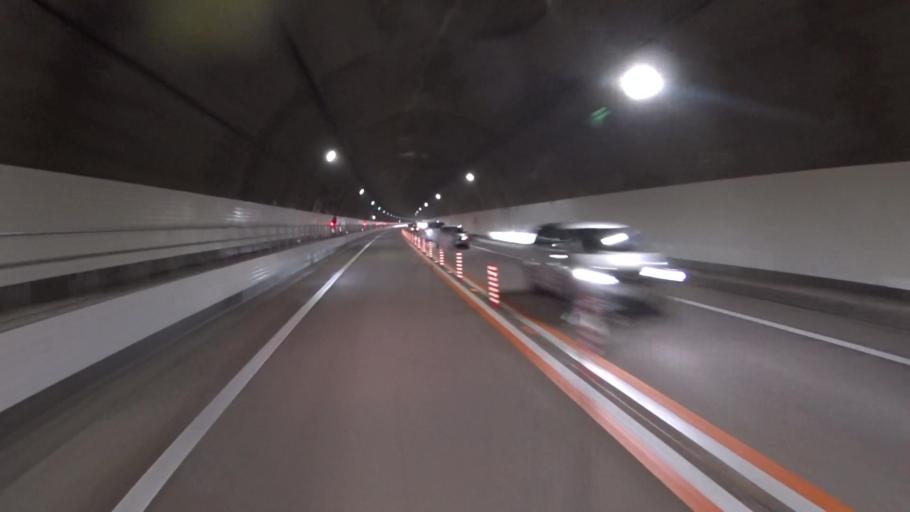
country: JP
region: Kyoto
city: Ayabe
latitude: 35.2385
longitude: 135.3435
